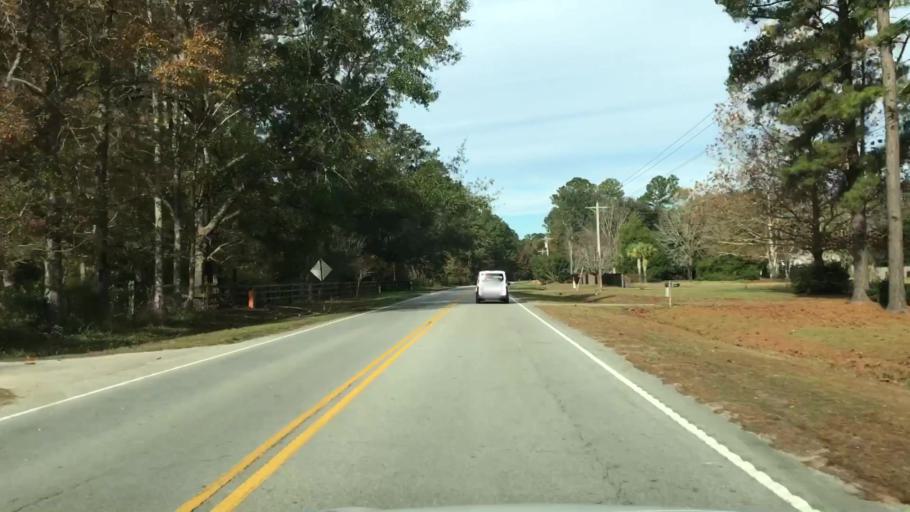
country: US
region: South Carolina
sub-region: Colleton County
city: Walterboro
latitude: 32.8595
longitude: -80.6030
